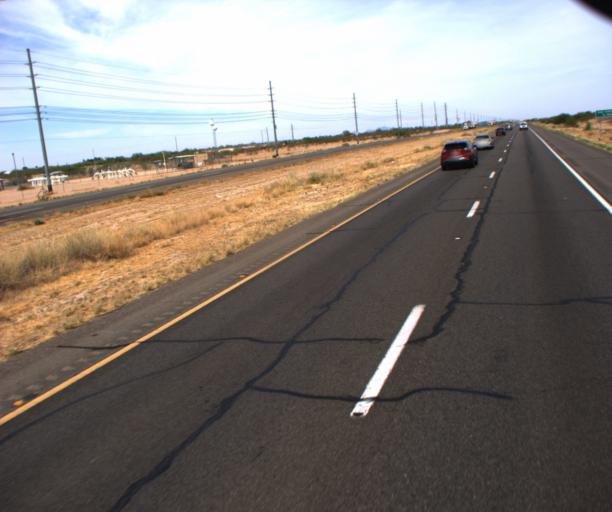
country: US
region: Arizona
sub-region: Maricopa County
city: Sun City West
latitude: 33.6926
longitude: -112.4192
